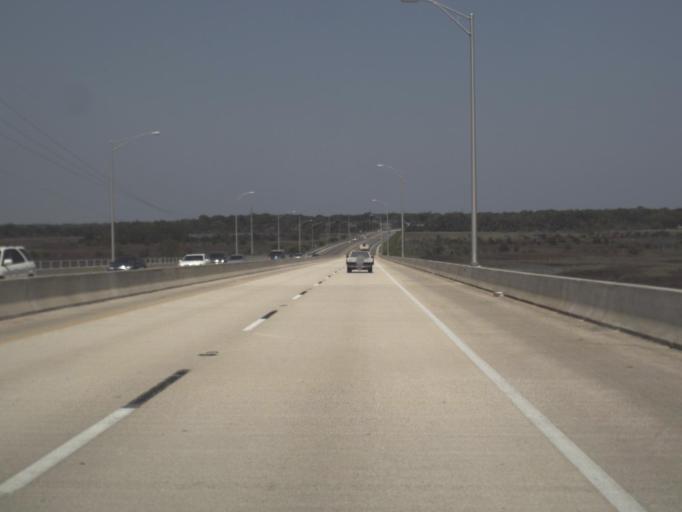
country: US
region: Florida
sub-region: Duval County
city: Atlantic Beach
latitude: 30.3620
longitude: -81.4399
